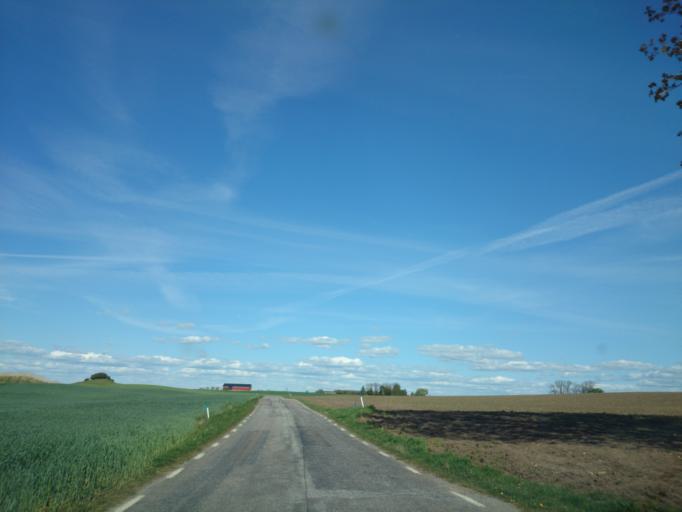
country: SE
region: Skane
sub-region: Kavlinge Kommun
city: Kaevlinge
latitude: 55.7845
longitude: 13.1206
